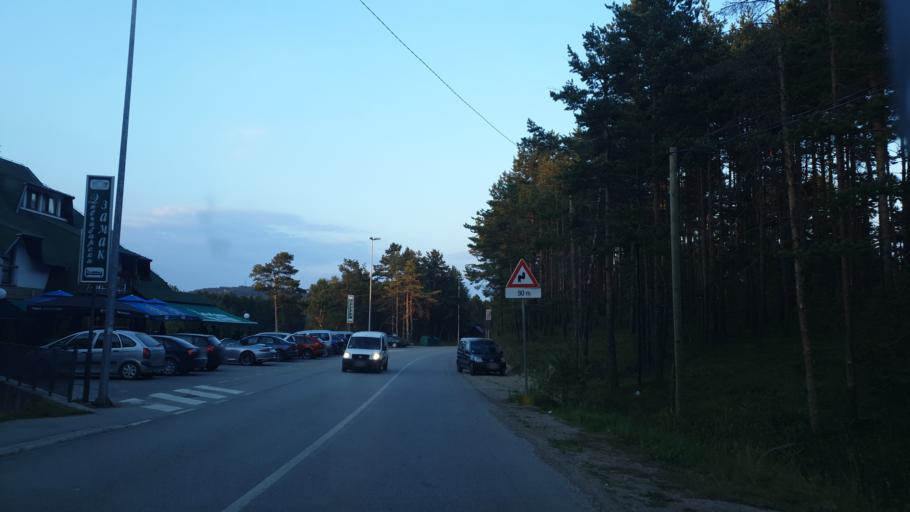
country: RS
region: Central Serbia
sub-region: Zlatiborski Okrug
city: Kosjeric
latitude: 44.1010
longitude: 19.9890
